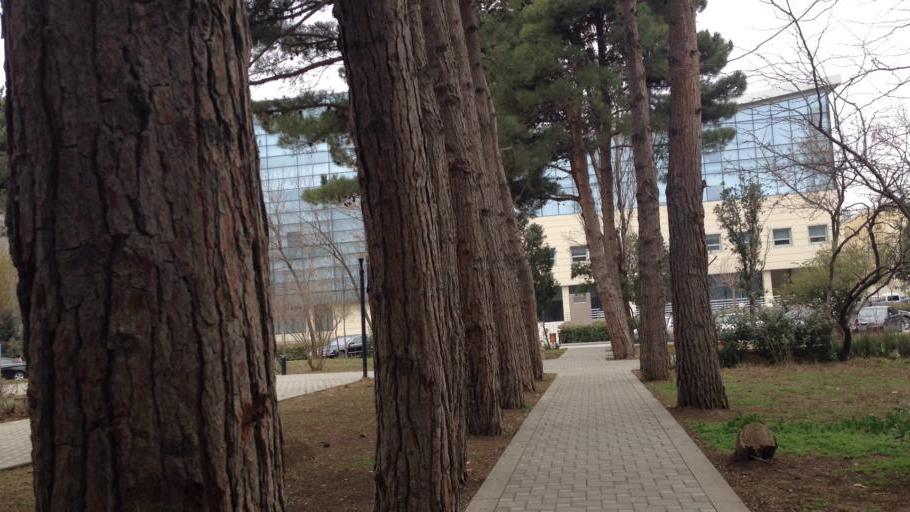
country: AZ
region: Baki
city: Badamdar
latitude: 40.3734
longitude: 49.8131
